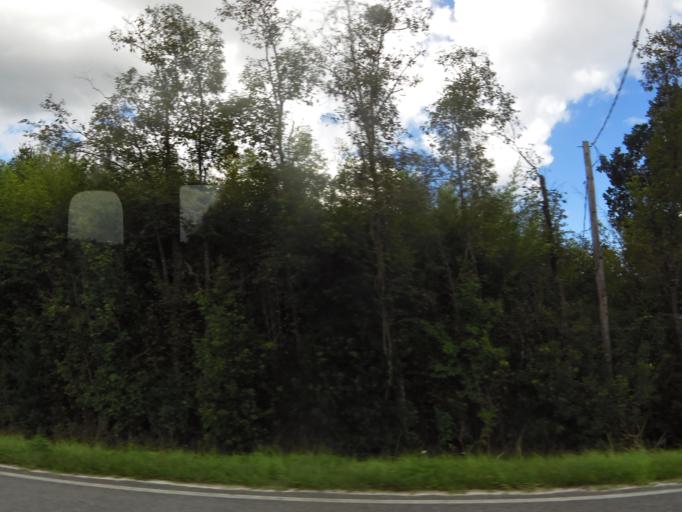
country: US
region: Florida
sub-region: Saint Johns County
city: Saint Augustine South
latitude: 29.8338
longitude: -81.4985
